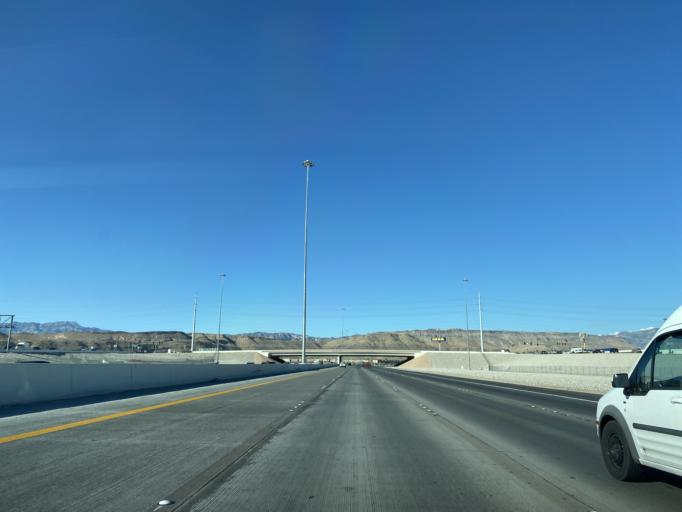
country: US
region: Nevada
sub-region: Clark County
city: Spring Valley
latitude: 36.0669
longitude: -115.2763
